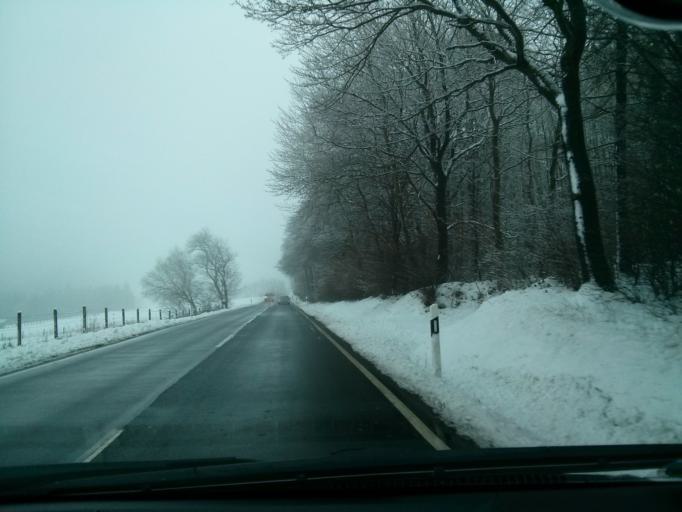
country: DE
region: Rheinland-Pfalz
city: Hummel
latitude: 50.5125
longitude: 6.8171
